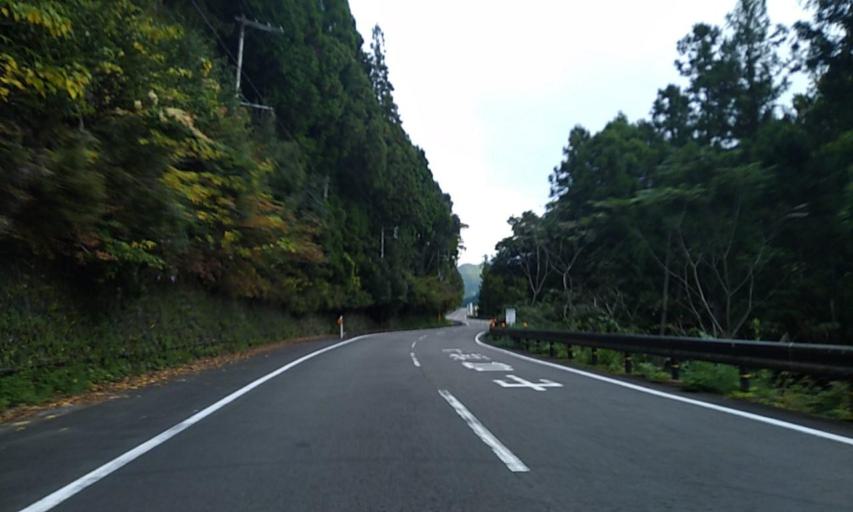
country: JP
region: Wakayama
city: Shingu
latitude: 33.9325
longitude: 135.9696
